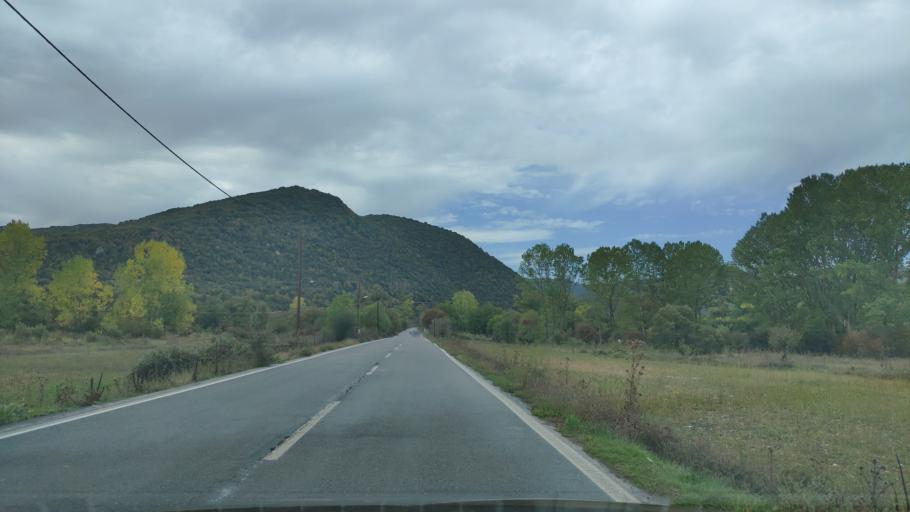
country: GR
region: Peloponnese
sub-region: Nomos Arkadias
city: Dimitsana
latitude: 37.6314
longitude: 22.0794
